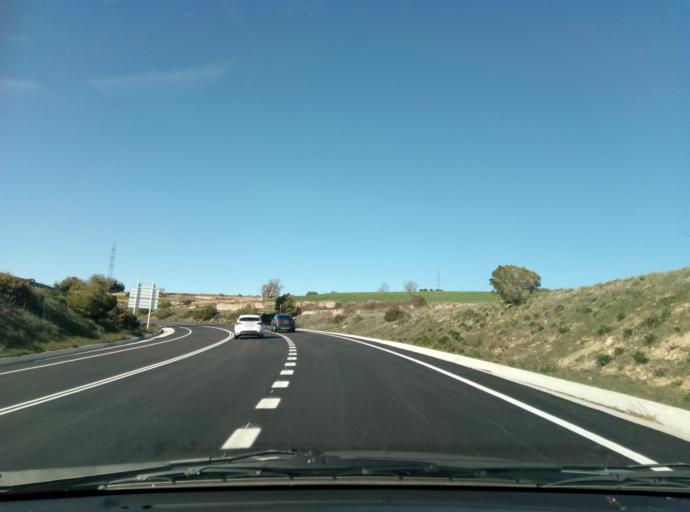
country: ES
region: Catalonia
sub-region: Provincia de Tarragona
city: Fores
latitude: 41.4896
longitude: 1.1927
